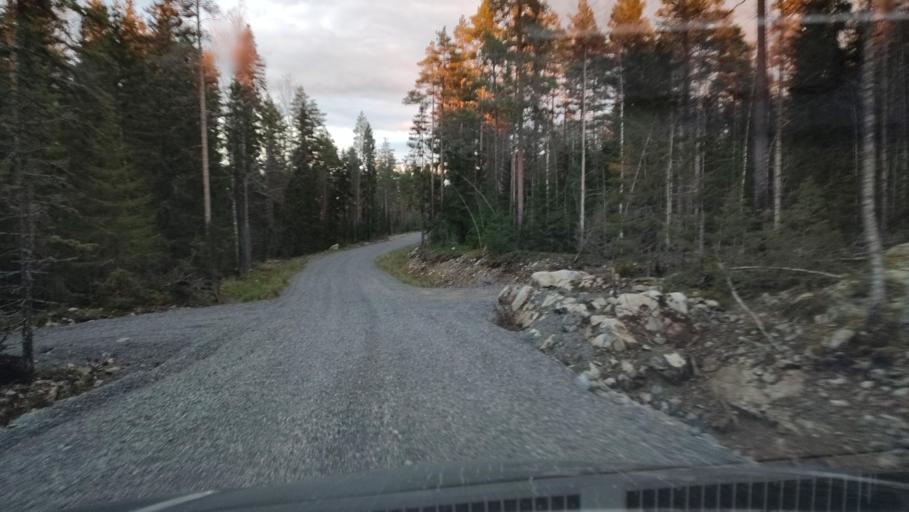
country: FI
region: Southern Ostrobothnia
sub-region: Suupohja
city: Karijoki
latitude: 62.2842
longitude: 21.6299
